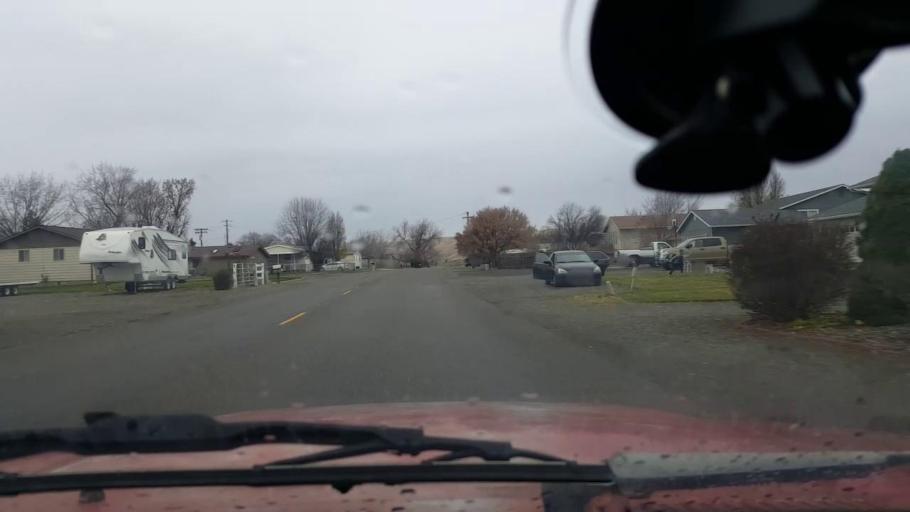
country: US
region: Washington
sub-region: Asotin County
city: Clarkston Heights-Vineland
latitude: 46.3832
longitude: -117.0857
